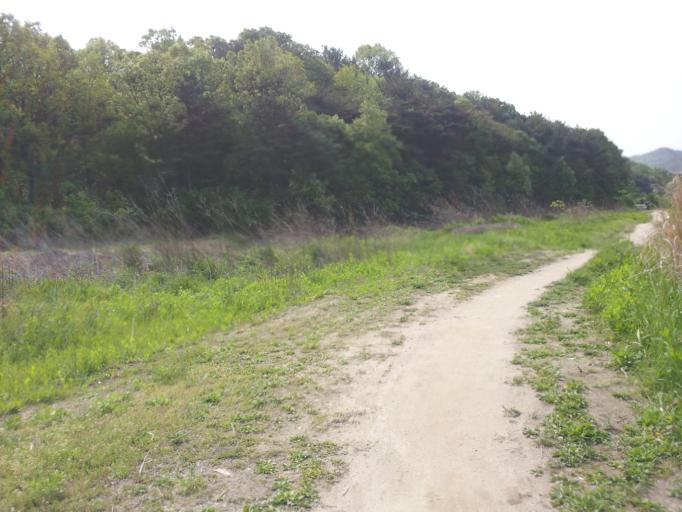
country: KR
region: Daejeon
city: Daejeon
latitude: 36.3363
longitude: 127.3545
